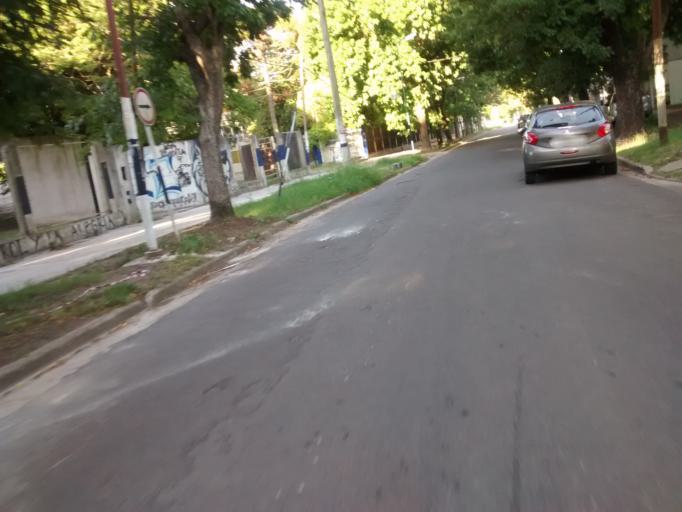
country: AR
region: Buenos Aires
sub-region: Partido de La Plata
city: La Plata
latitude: -34.9130
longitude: -57.9309
